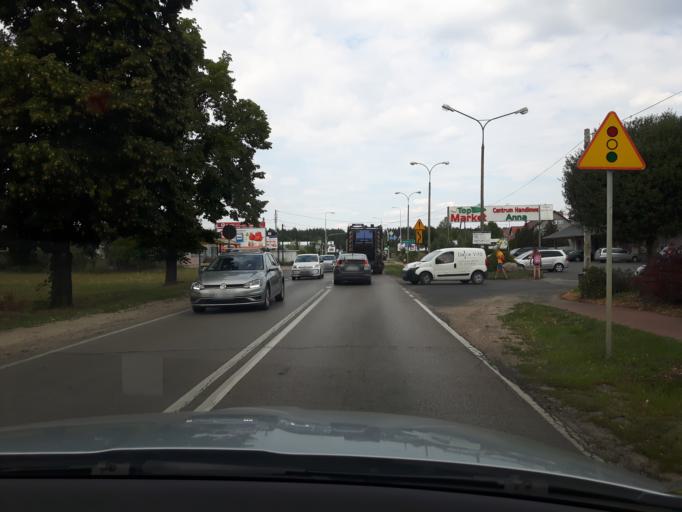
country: PL
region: Masovian Voivodeship
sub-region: Powiat legionowski
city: Stanislawow Pierwszy
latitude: 52.3966
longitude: 21.0349
